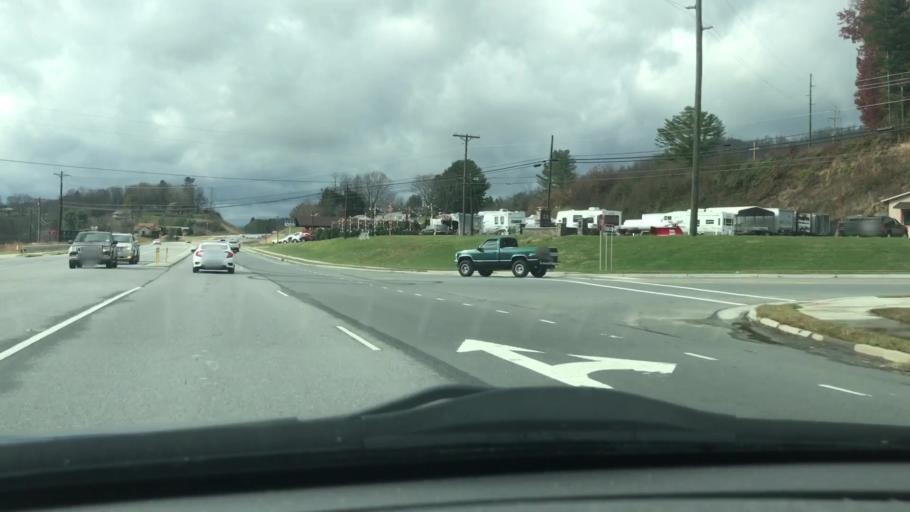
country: US
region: North Carolina
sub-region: Yancey County
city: Burnsville
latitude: 35.9127
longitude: -82.3148
